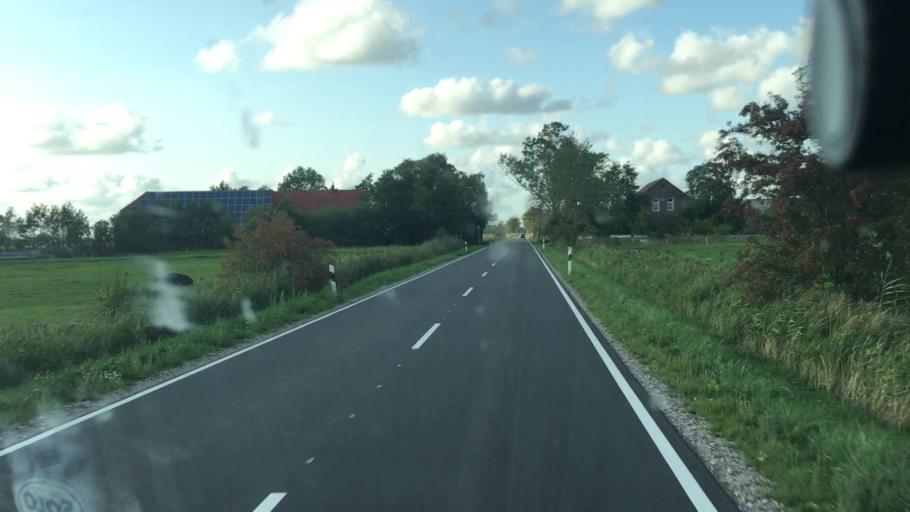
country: DE
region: Lower Saxony
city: Jever
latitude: 53.6203
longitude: 7.8646
